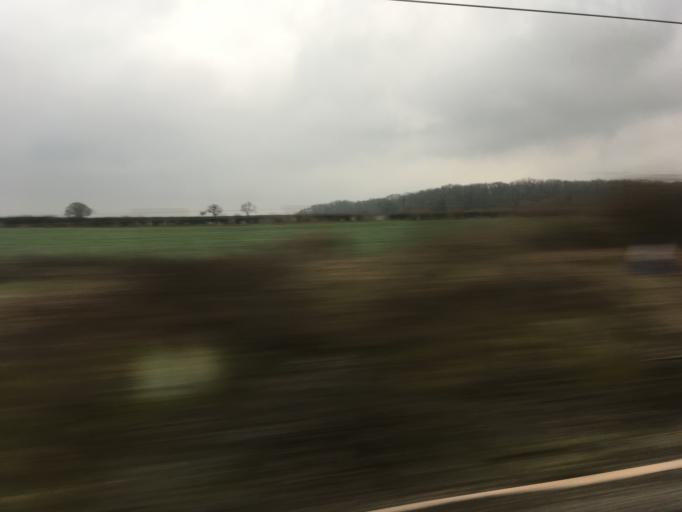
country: GB
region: England
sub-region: Wiltshire
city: Norton
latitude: 51.5451
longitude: -2.1906
